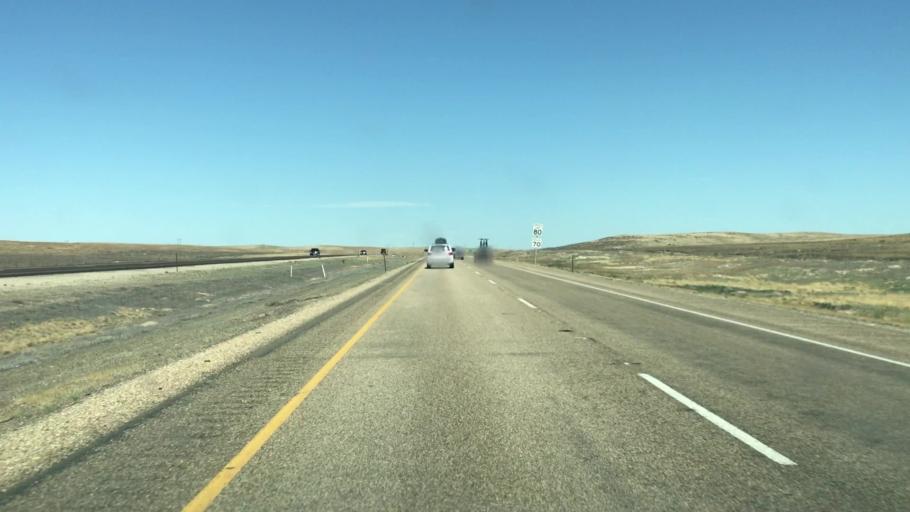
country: US
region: Idaho
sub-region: Payette County
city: New Plymouth
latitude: 43.8714
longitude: -116.7859
